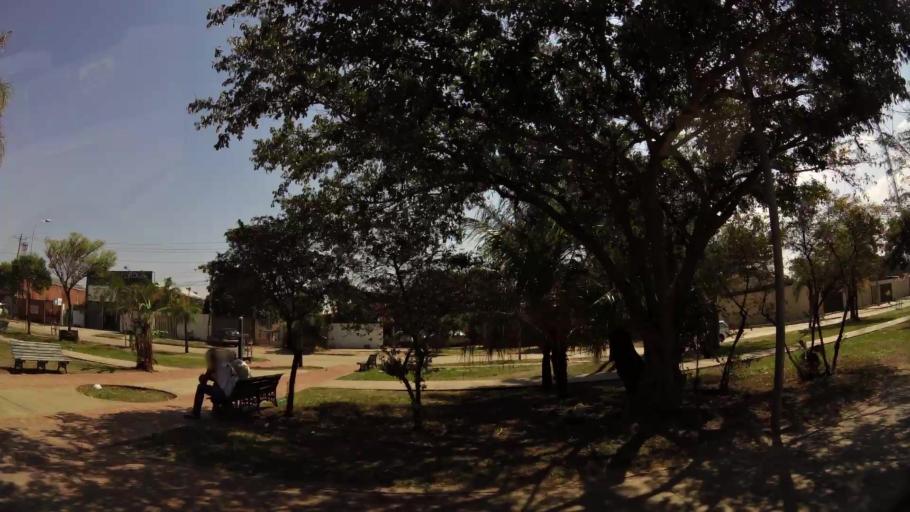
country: BO
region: Santa Cruz
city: Santa Cruz de la Sierra
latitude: -17.7355
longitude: -63.1530
